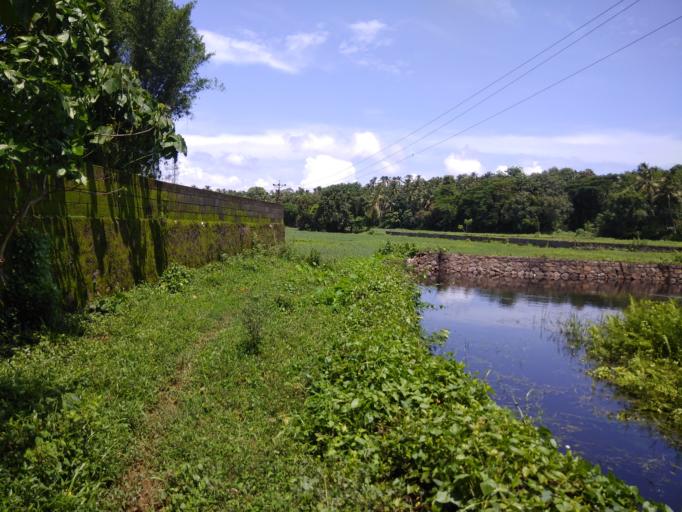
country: IN
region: Kerala
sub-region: Thrissur District
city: Trichur
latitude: 10.5514
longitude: 76.1760
